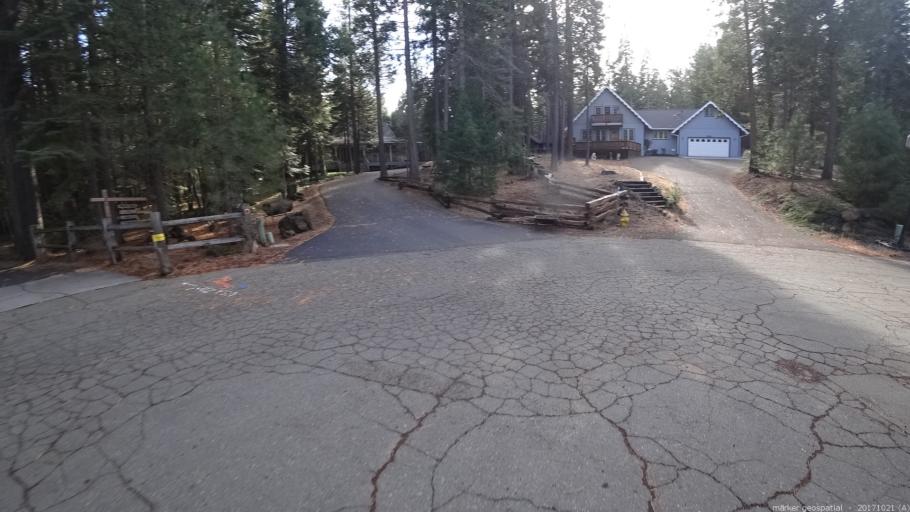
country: US
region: California
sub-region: Shasta County
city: Burney
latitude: 40.8706
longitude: -121.6693
